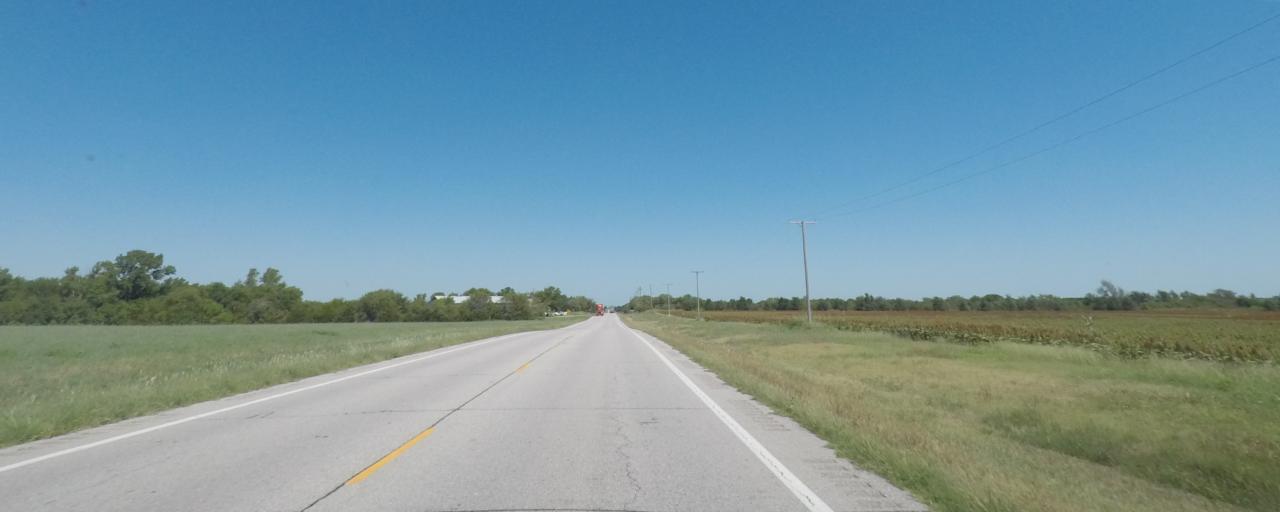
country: US
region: Kansas
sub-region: Sumner County
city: Wellington
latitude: 37.3676
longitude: -97.3850
